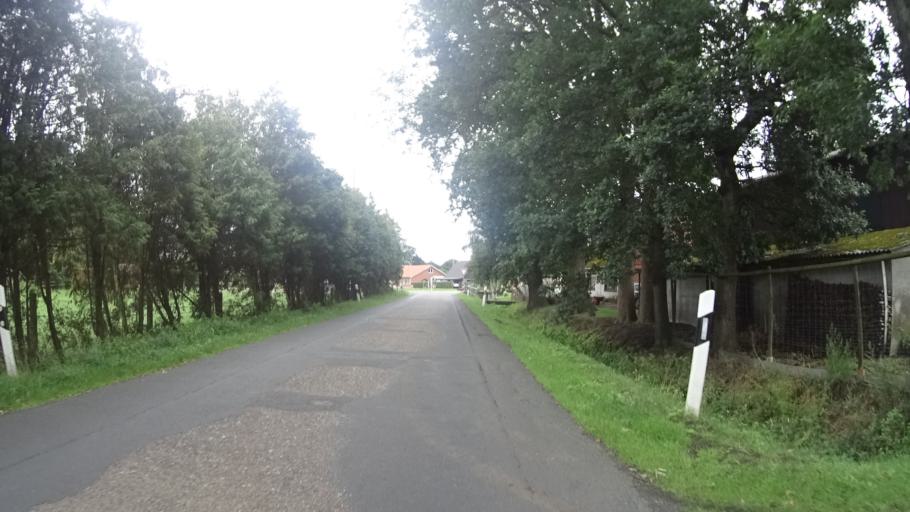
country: DE
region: Lower Saxony
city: Stinstedt
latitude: 53.6355
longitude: 8.9587
